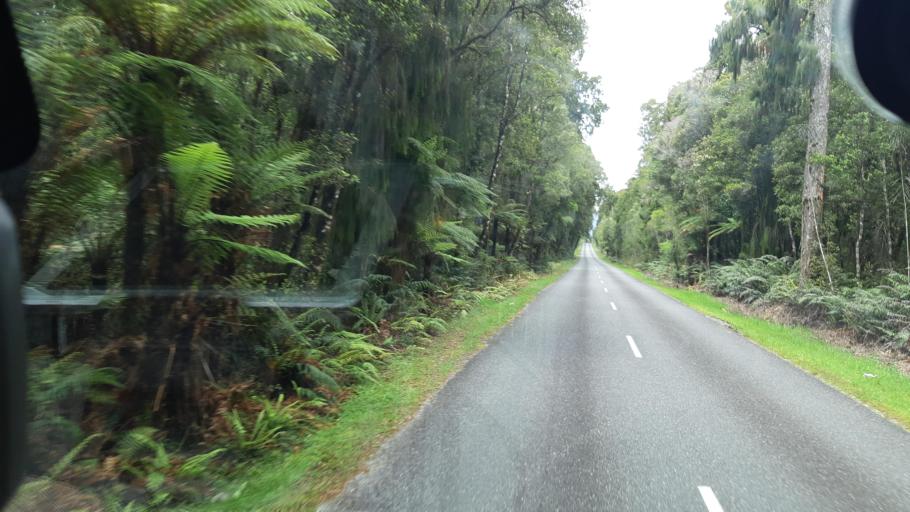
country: NZ
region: West Coast
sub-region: Westland District
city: Hokitika
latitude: -42.7762
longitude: 171.0948
